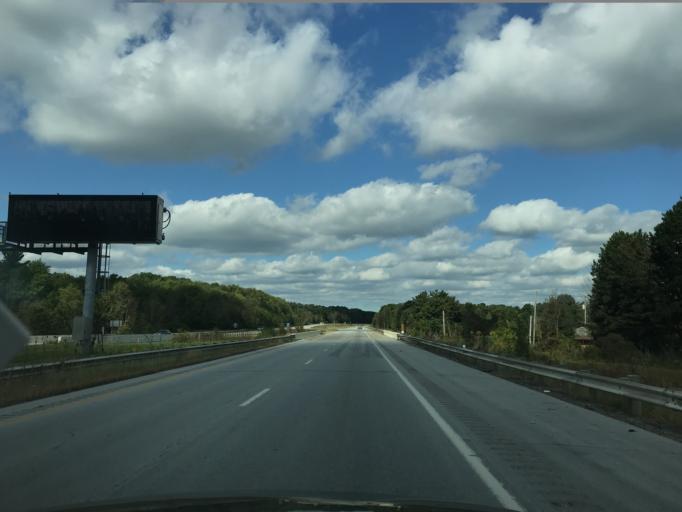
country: US
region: Ohio
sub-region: Summit County
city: Twinsburg
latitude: 41.2761
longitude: -81.4086
